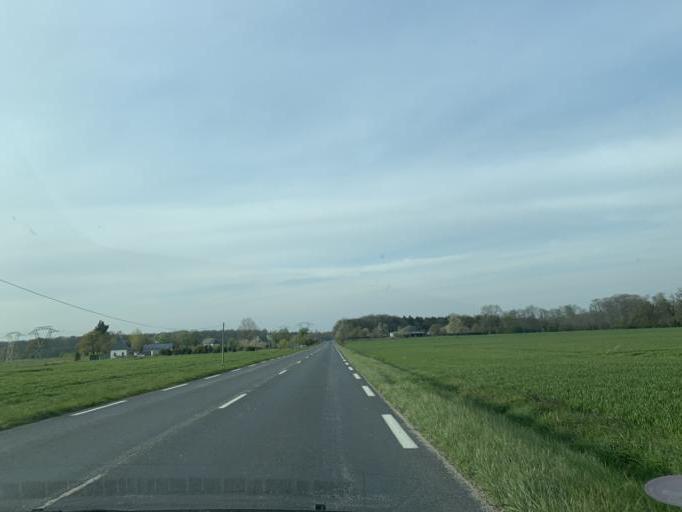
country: FR
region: Haute-Normandie
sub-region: Departement de l'Eure
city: Hauville
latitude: 49.4074
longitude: 0.7969
